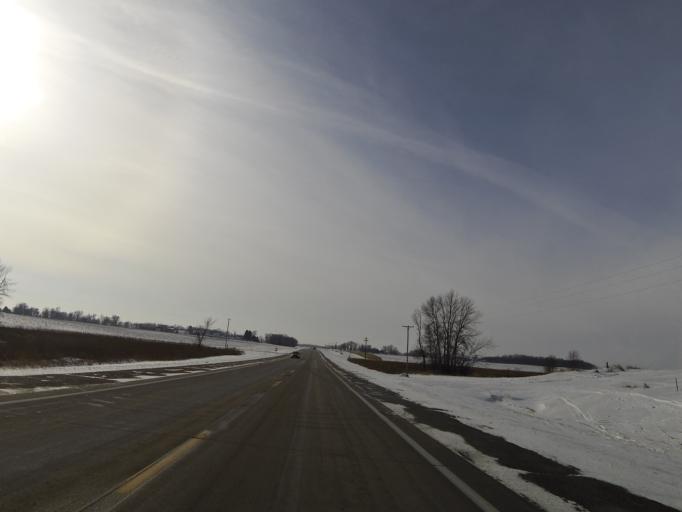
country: US
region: Minnesota
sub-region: McLeod County
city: Glencoe
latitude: 44.8998
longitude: -94.2173
